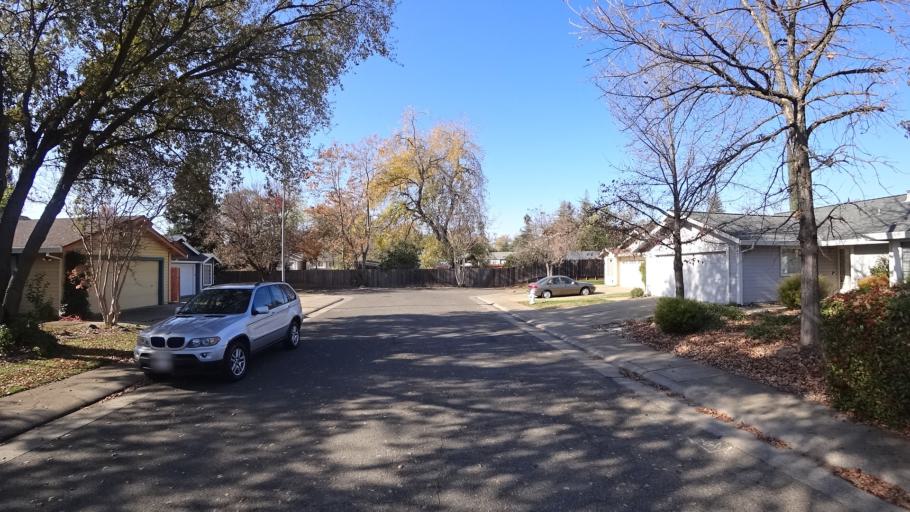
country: US
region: California
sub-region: Sacramento County
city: Citrus Heights
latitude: 38.6966
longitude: -121.2841
